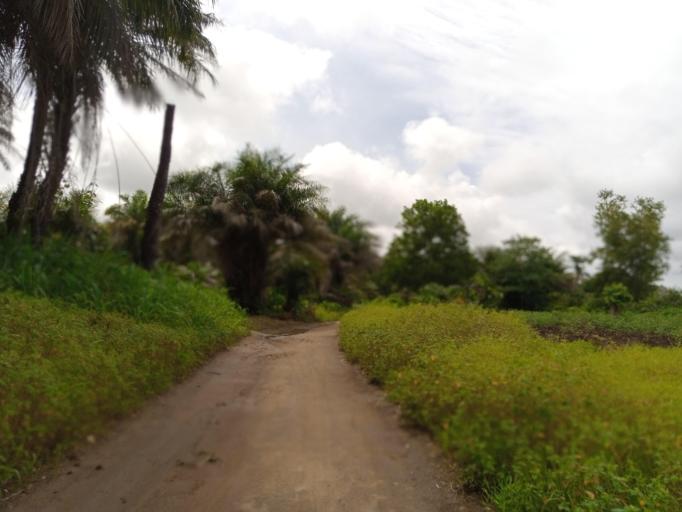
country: SL
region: Northern Province
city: Masoyila
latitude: 8.5884
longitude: -13.1944
